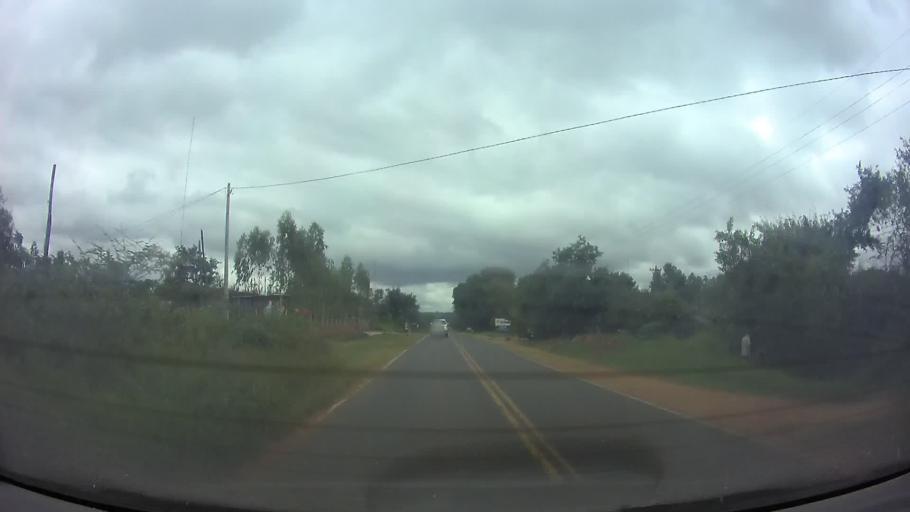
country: PY
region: Central
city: Guarambare
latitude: -25.5042
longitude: -57.4831
